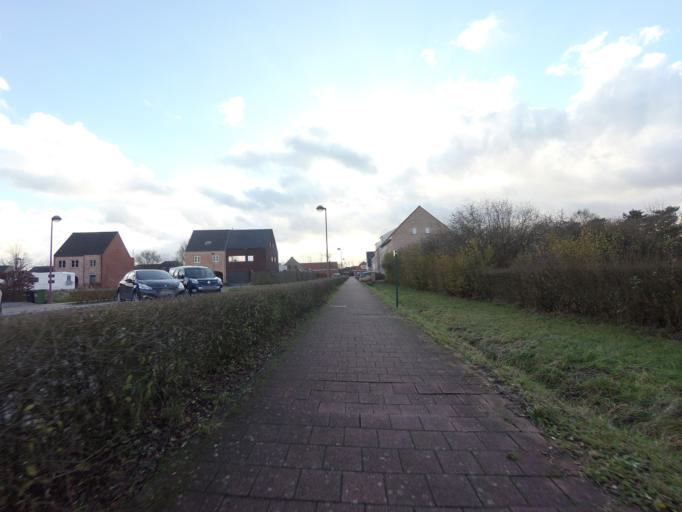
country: BE
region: Flanders
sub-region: Provincie Antwerpen
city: Lint
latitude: 51.1267
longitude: 4.5095
